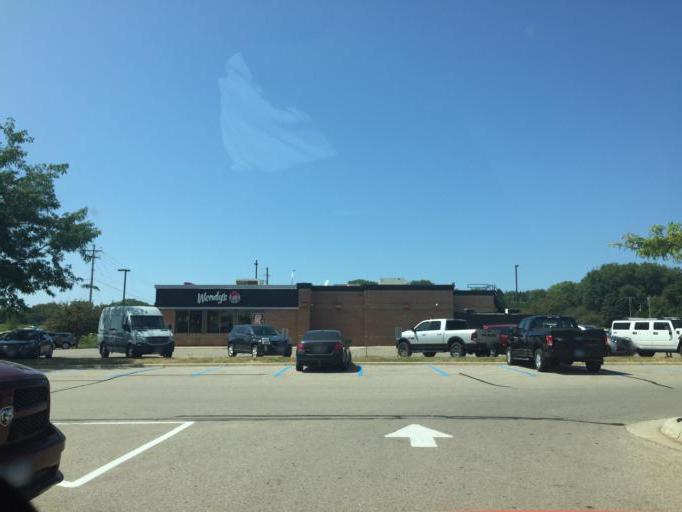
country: US
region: Minnesota
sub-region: Olmsted County
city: Rochester
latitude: 43.9787
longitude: -92.4610
